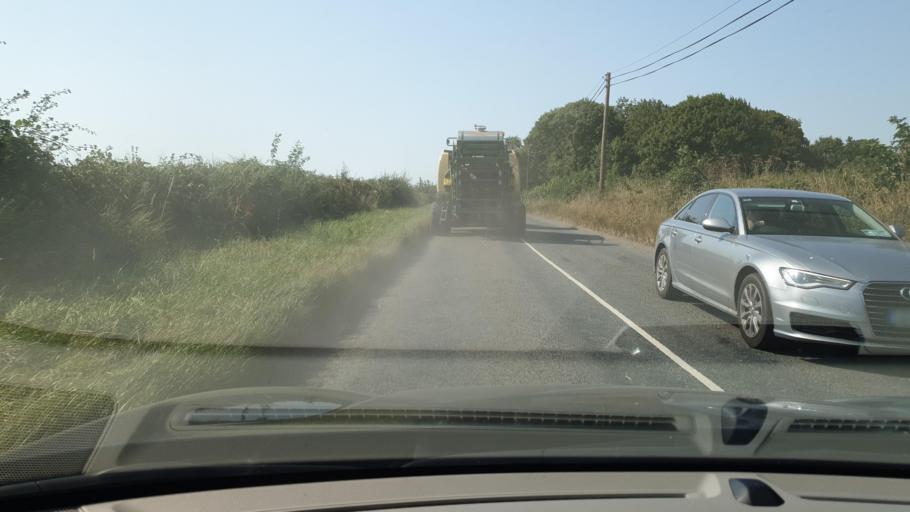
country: IE
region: Leinster
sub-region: An Mhi
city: Athboy
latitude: 53.6132
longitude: -6.8992
